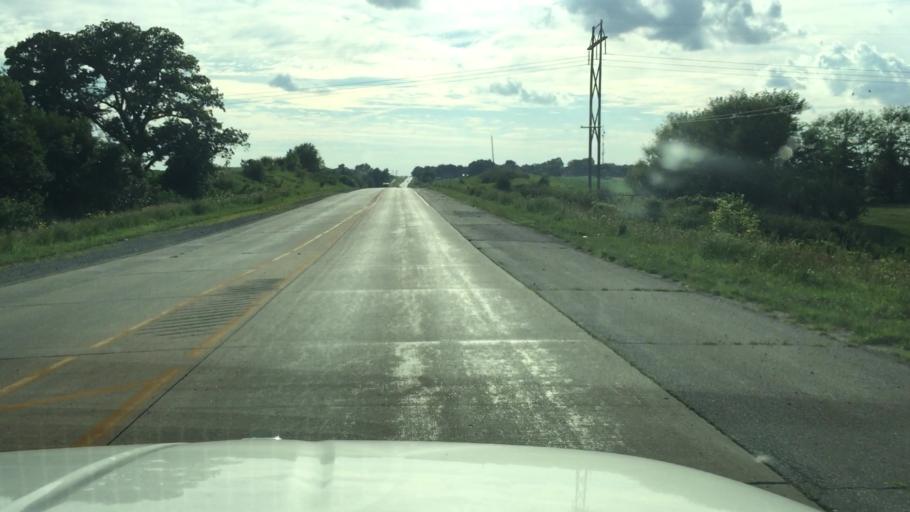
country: US
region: Iowa
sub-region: Johnson County
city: Iowa City
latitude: 41.6710
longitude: -91.4570
